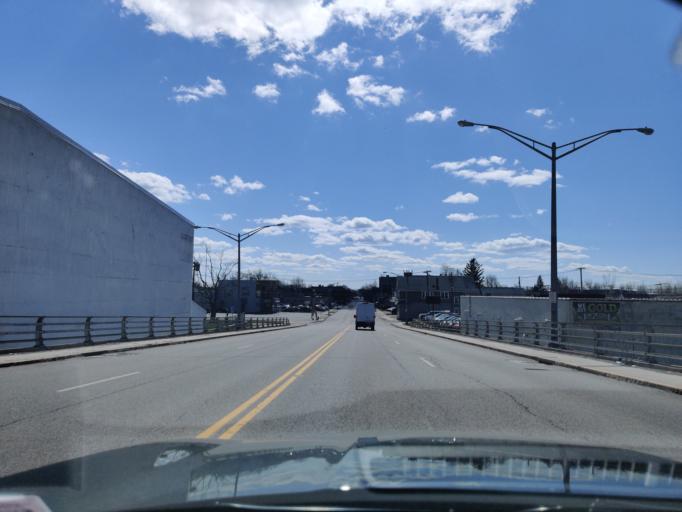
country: US
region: New York
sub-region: Erie County
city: Sloan
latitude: 42.8931
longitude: -78.8142
